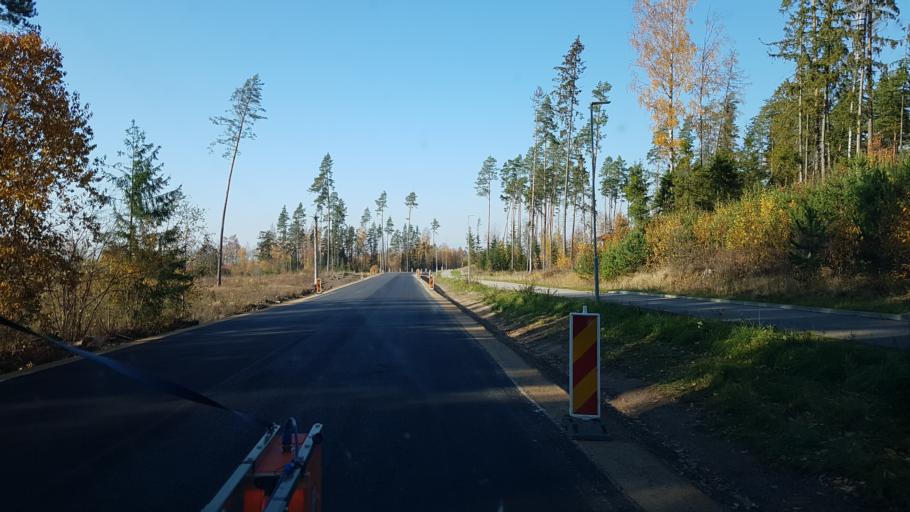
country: EE
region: Vorumaa
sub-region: Antsla vald
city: Vana-Antsla
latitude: 57.8320
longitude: 26.5107
